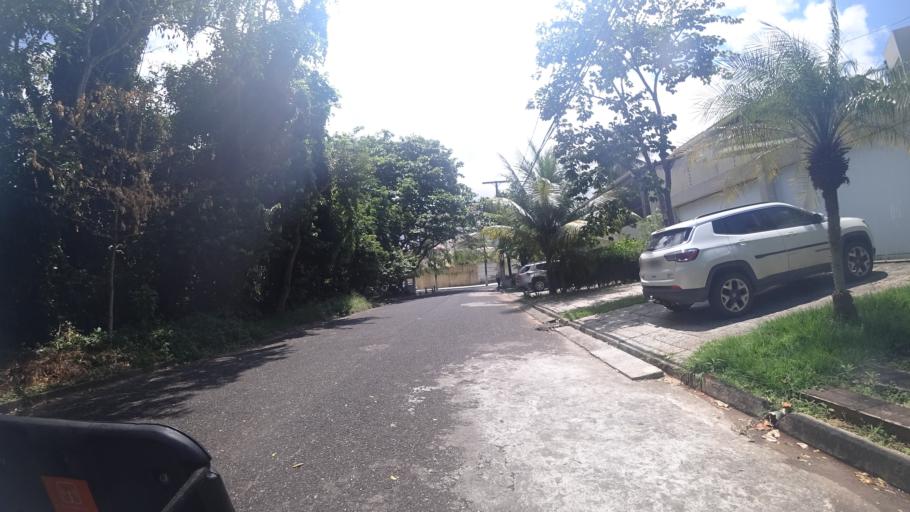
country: BR
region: Bahia
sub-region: Salvador
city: Salvador
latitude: -12.9933
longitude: -38.4698
